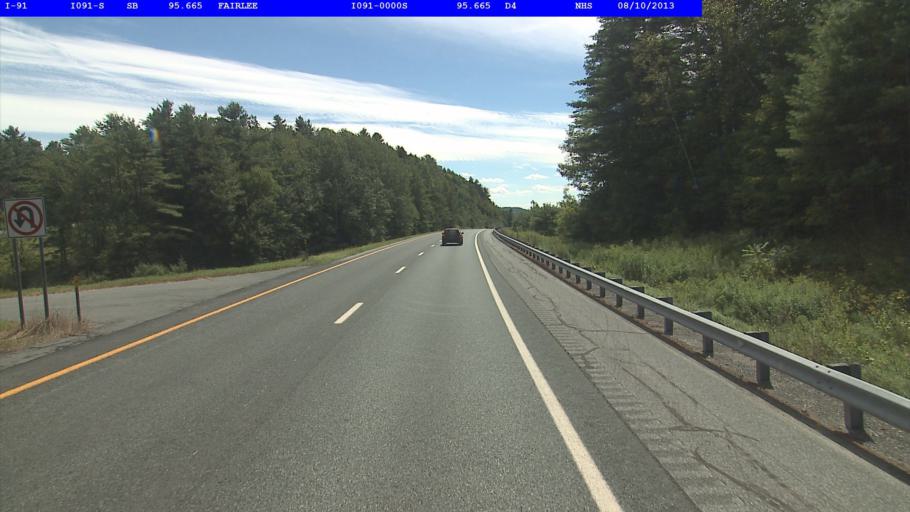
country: US
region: New Hampshire
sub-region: Grafton County
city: Orford
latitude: 43.9571
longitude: -72.1301
